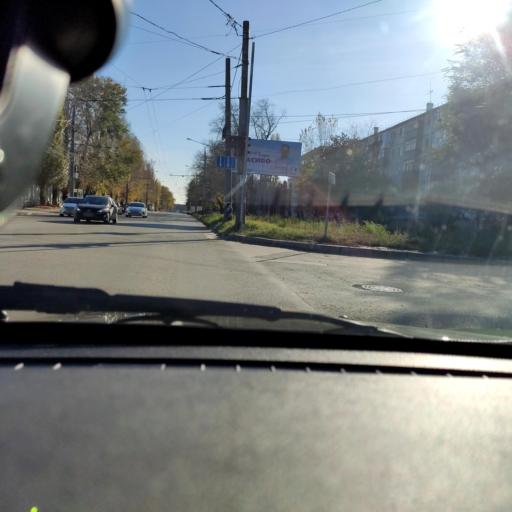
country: RU
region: Samara
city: Tol'yatti
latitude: 53.5146
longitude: 49.4290
